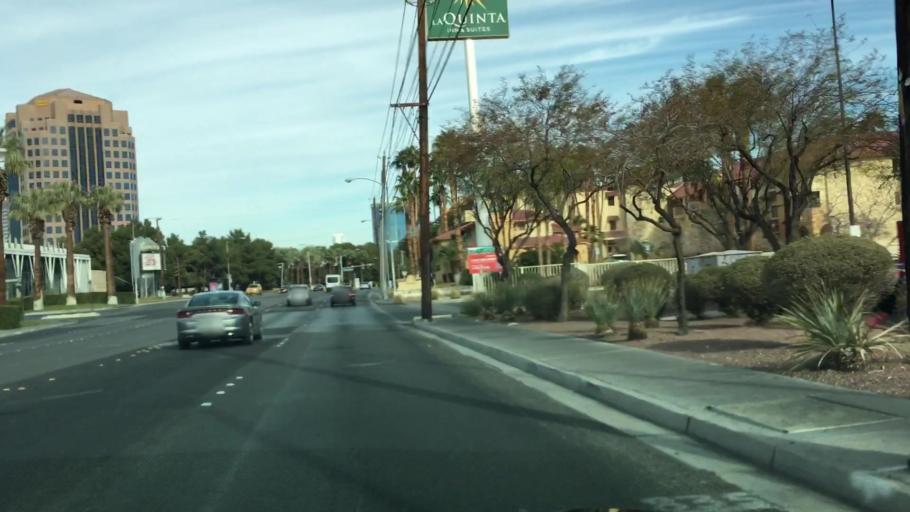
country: US
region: Nevada
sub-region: Clark County
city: Paradise
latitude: 36.1161
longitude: -115.1544
